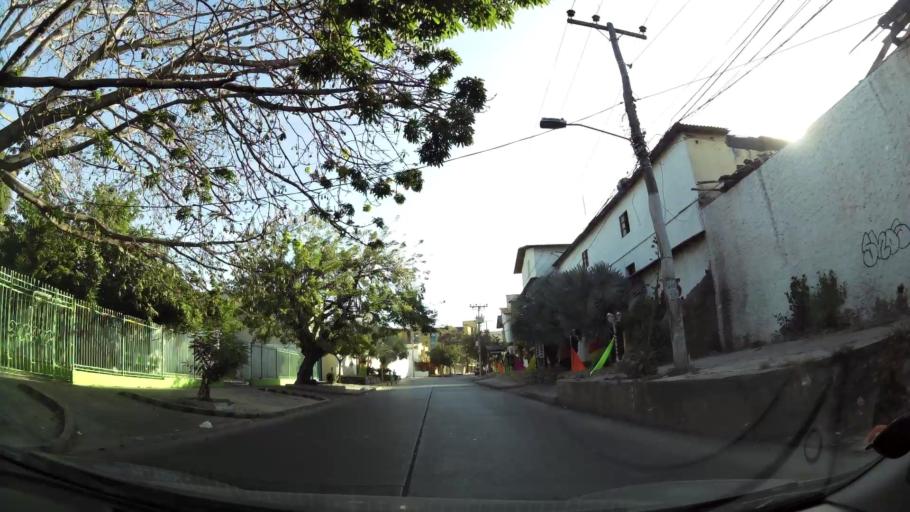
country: CO
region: Atlantico
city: Barranquilla
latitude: 10.9857
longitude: -74.7920
